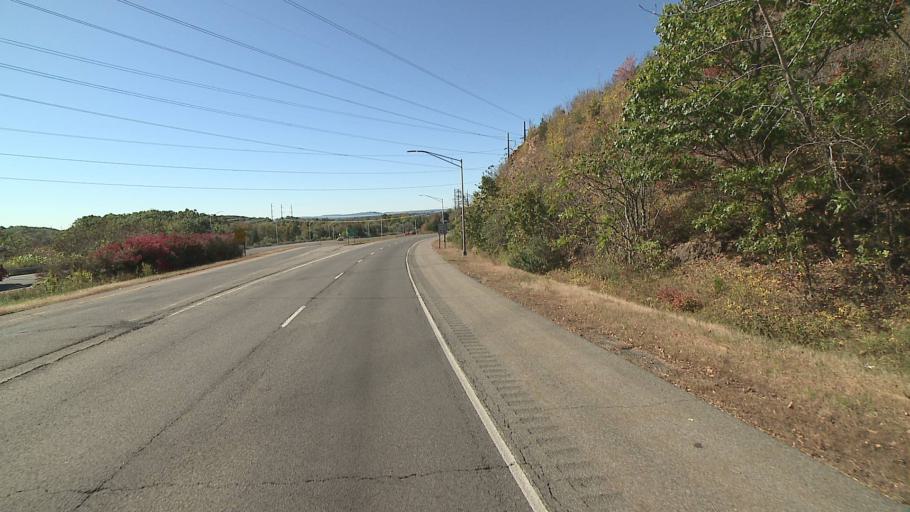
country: US
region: Connecticut
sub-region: New Haven County
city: Meriden
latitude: 41.5289
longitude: -72.7425
